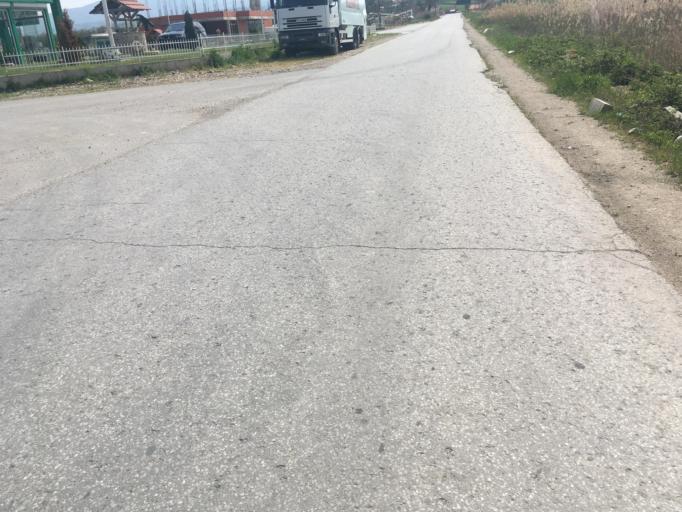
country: MK
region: Karbinci
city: Karbinci
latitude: 41.8001
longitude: 22.2187
